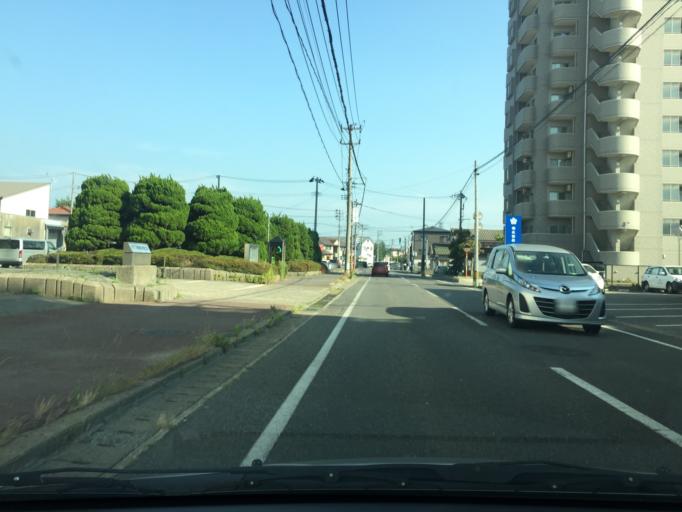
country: JP
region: Niigata
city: Niigata-shi
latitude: 37.8888
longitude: 139.0402
